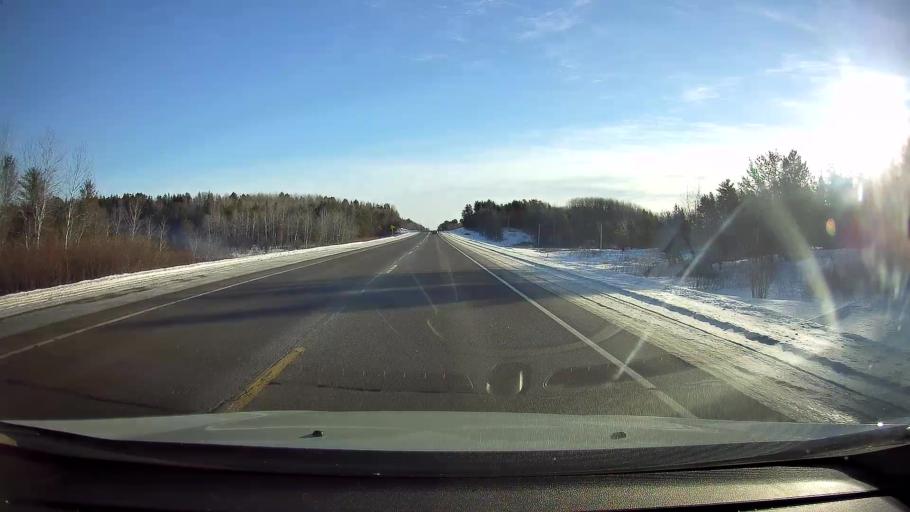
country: US
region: Wisconsin
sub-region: Washburn County
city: Spooner
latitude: 45.9104
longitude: -91.7918
